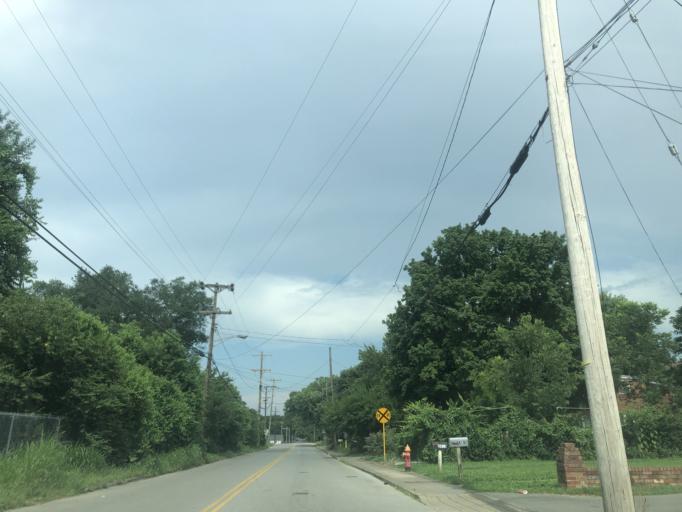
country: US
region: Tennessee
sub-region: Davidson County
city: Nashville
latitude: 36.1703
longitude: -86.8157
